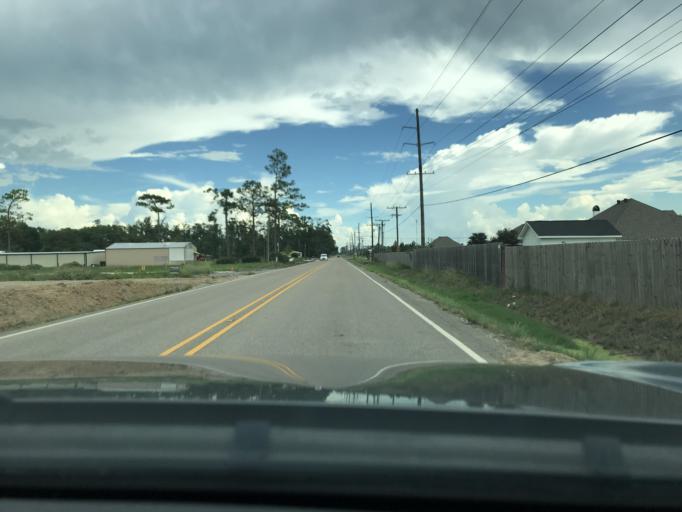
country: US
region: Louisiana
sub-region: Calcasieu Parish
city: Moss Bluff
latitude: 30.3385
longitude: -93.2329
